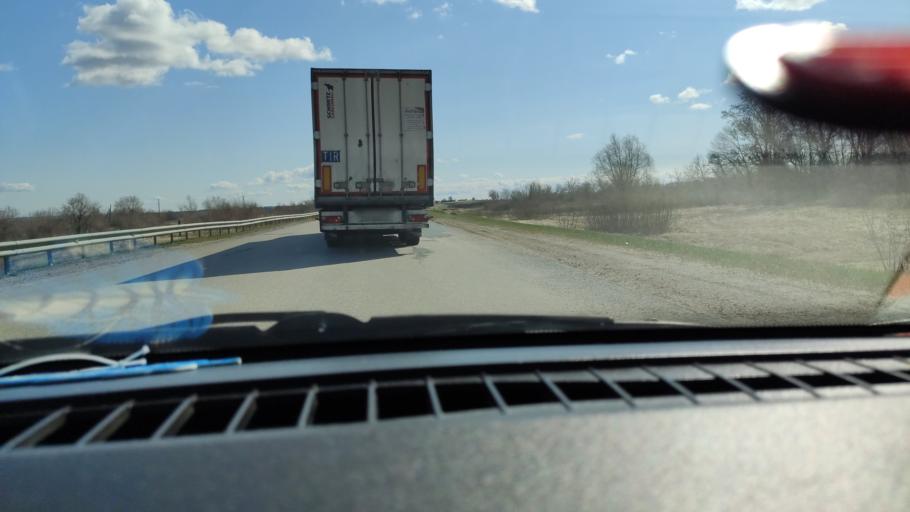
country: RU
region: Samara
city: Varlamovo
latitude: 53.1211
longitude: 48.3234
